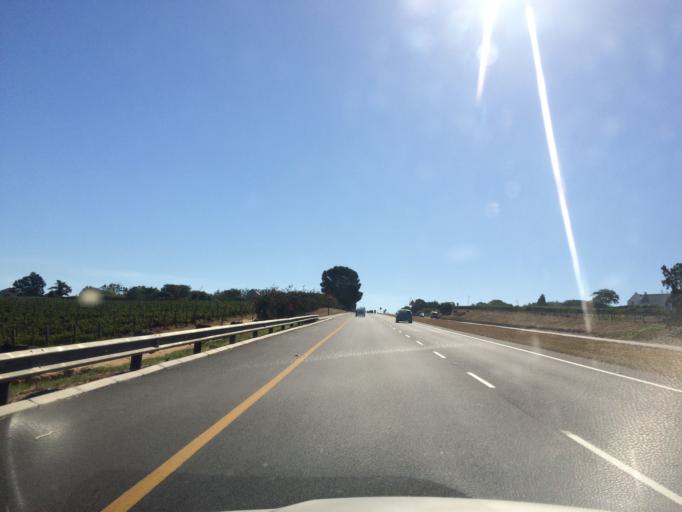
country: ZA
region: Western Cape
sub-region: City of Cape Town
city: Kraaifontein
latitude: -33.9630
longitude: 18.7383
